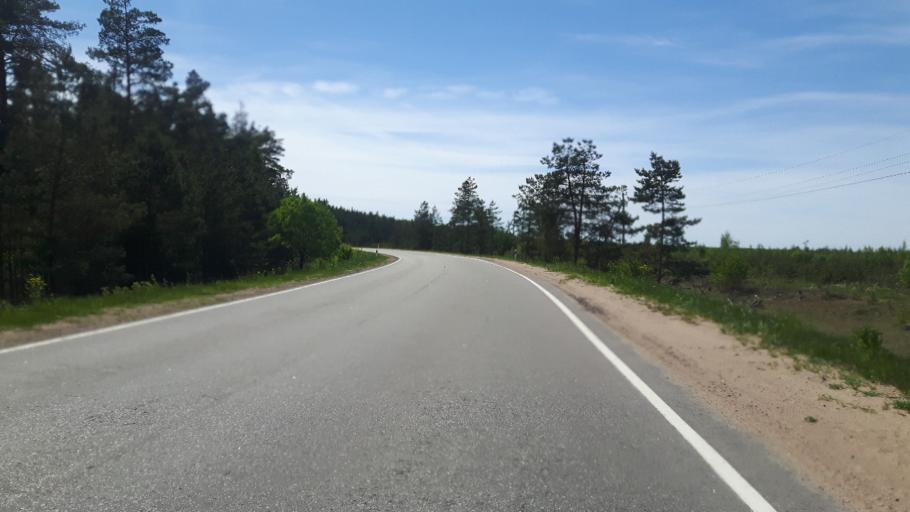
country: EE
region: Ida-Virumaa
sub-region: Narva-Joesuu linn
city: Narva-Joesuu
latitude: 59.5702
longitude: 28.1551
